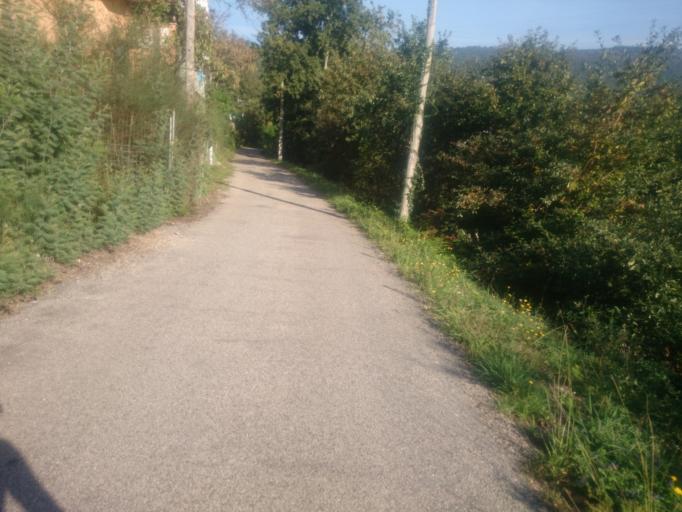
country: ES
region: Galicia
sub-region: Provincia de Pontevedra
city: Porrino
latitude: 42.1580
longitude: -8.6078
